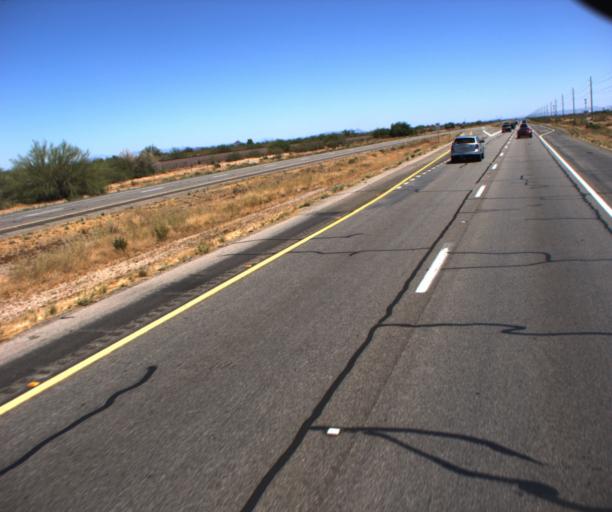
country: US
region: Arizona
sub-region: Maricopa County
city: Sun City West
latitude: 33.7634
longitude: -112.5103
